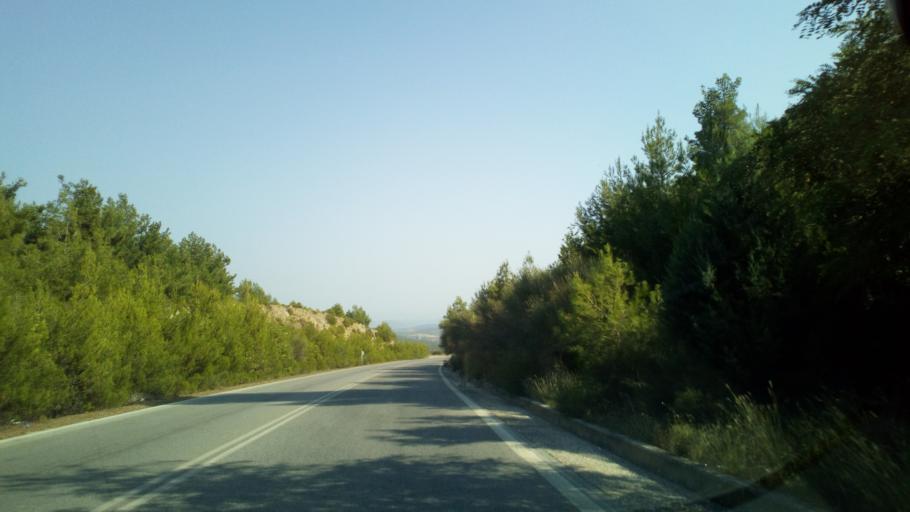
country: GR
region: Central Macedonia
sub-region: Nomos Chalkidikis
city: Polygyros
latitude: 40.3520
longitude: 23.4457
